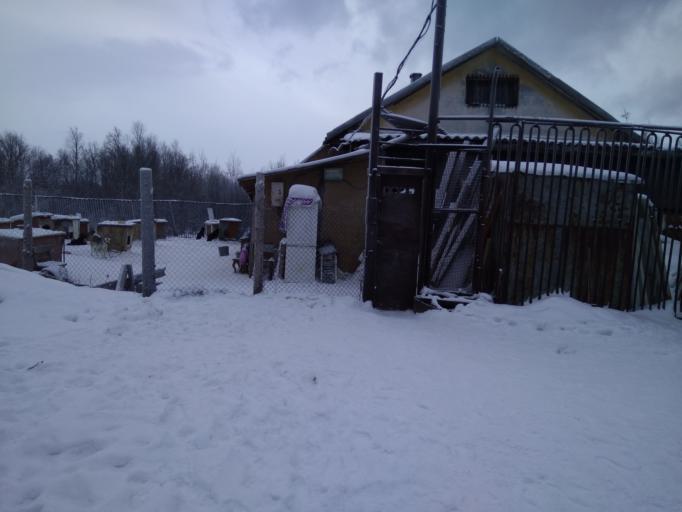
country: RU
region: Murmansk
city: Revda
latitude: 67.9461
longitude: 34.5630
